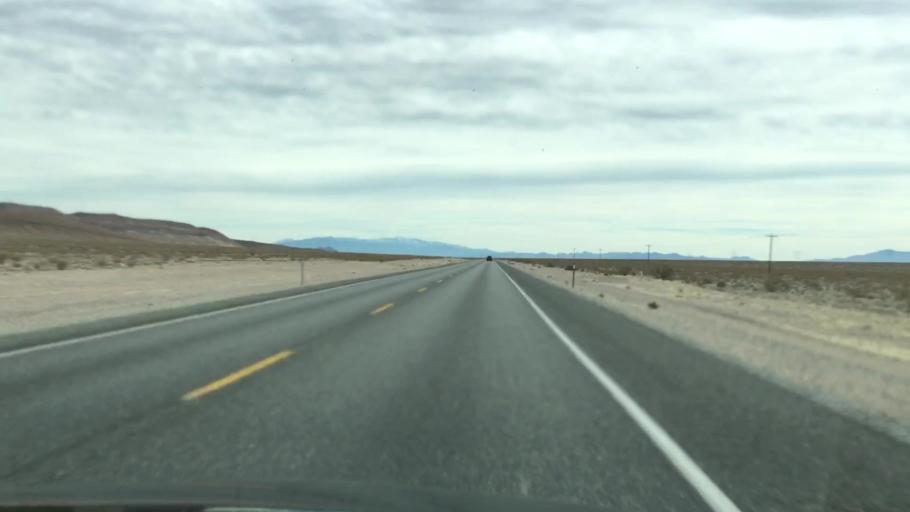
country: US
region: Nevada
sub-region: Nye County
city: Beatty
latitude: 36.7004
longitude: -116.5820
